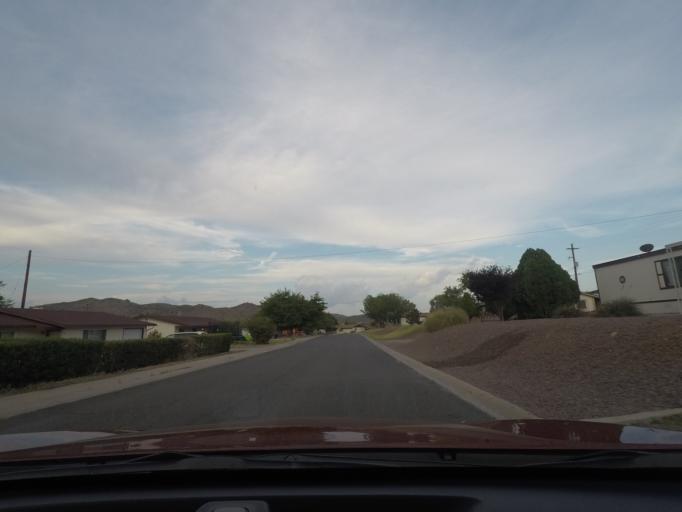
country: US
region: Arizona
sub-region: Yavapai County
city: Bagdad
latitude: 34.5718
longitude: -113.1805
